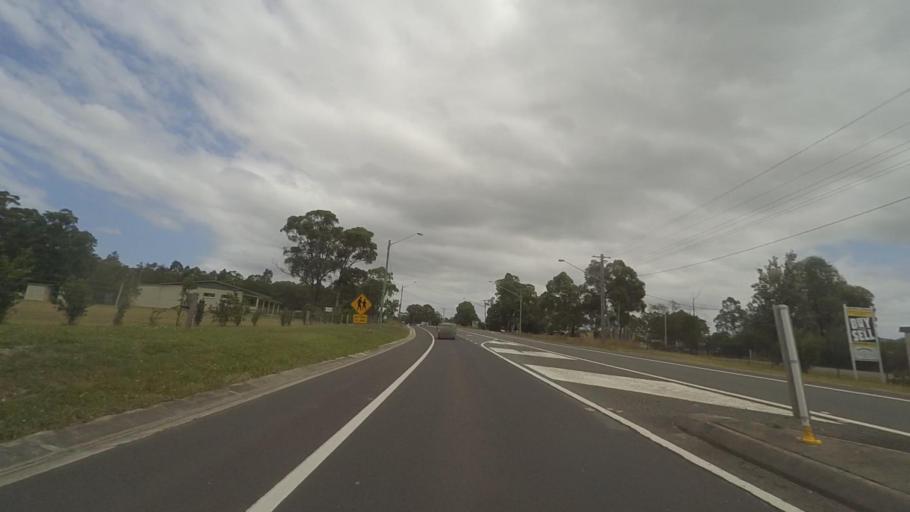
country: AU
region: New South Wales
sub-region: Shoalhaven Shire
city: Falls Creek
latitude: -35.0881
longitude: 150.5114
